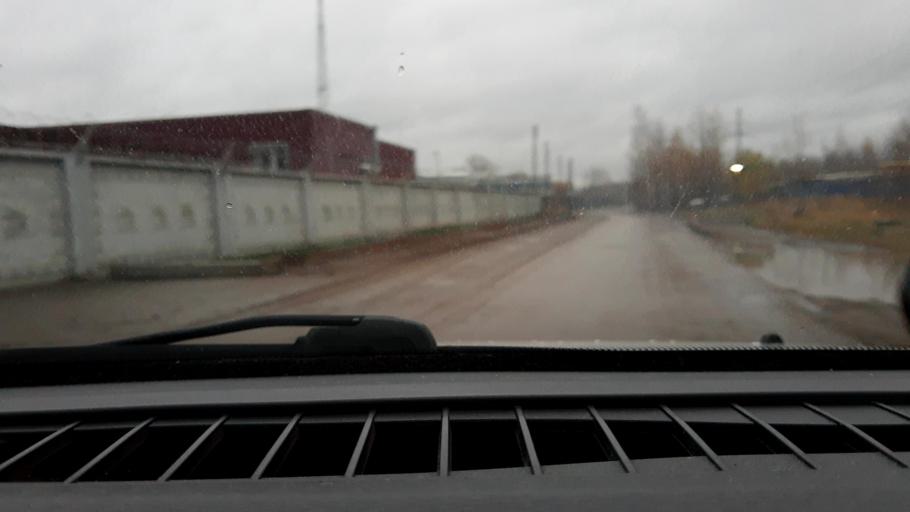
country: RU
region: Nizjnij Novgorod
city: Gorbatovka
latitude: 56.2732
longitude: 43.8525
